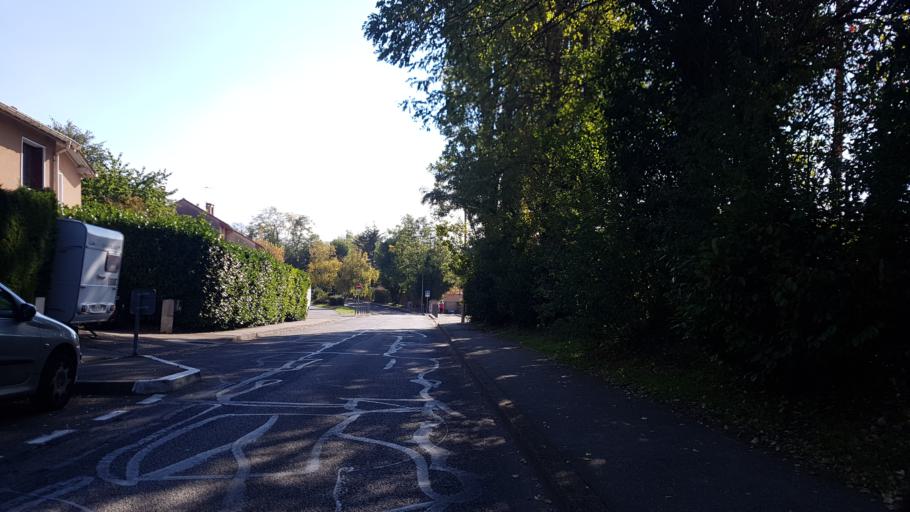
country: FR
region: Rhone-Alpes
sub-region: Departement du Rhone
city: Ecully
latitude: 45.7976
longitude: 4.7792
